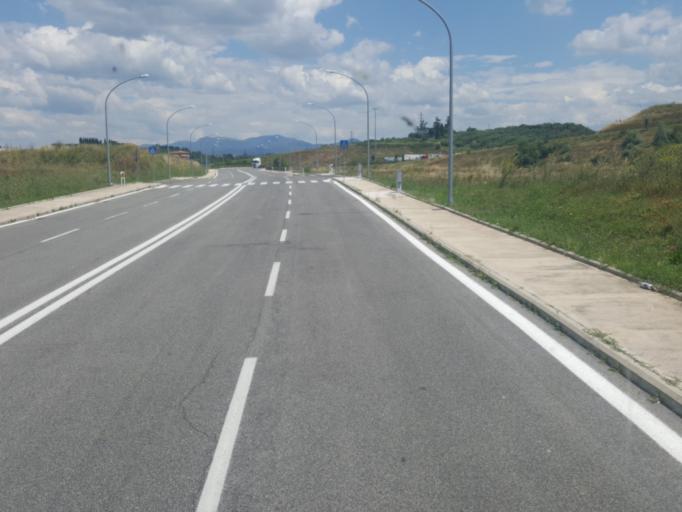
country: IT
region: Latium
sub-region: Citta metropolitana di Roma Capitale
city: Fiano Romano
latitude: 42.1636
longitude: 12.6476
